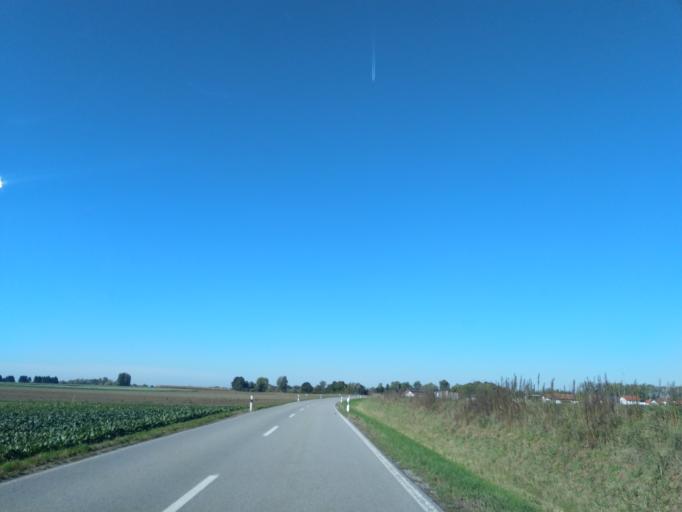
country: DE
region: Bavaria
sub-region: Lower Bavaria
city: Offenberg
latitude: 48.8222
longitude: 12.8718
